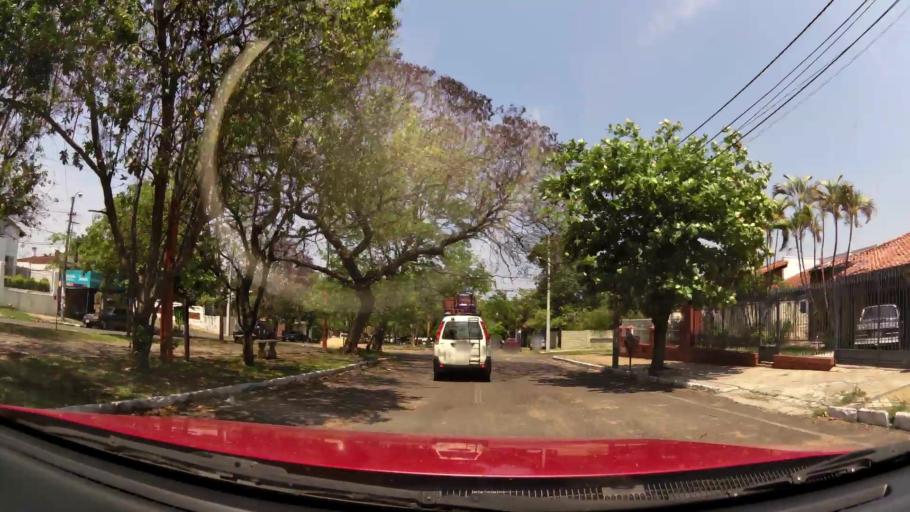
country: PY
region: Asuncion
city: Asuncion
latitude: -25.3055
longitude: -57.6481
